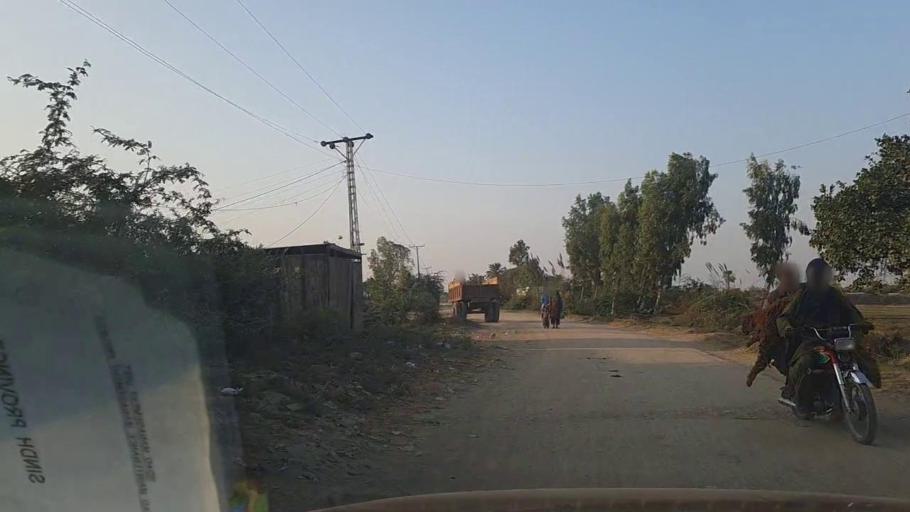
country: PK
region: Sindh
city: Keti Bandar
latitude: 24.3055
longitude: 67.6041
